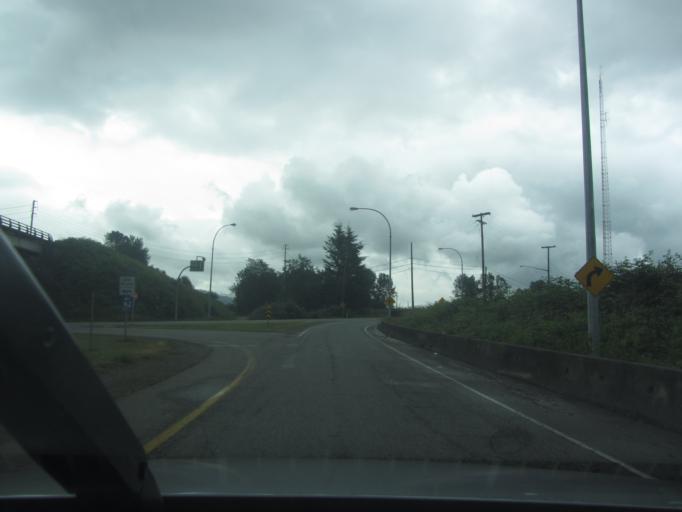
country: CA
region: British Columbia
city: Abbotsford
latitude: 49.1170
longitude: -122.2949
